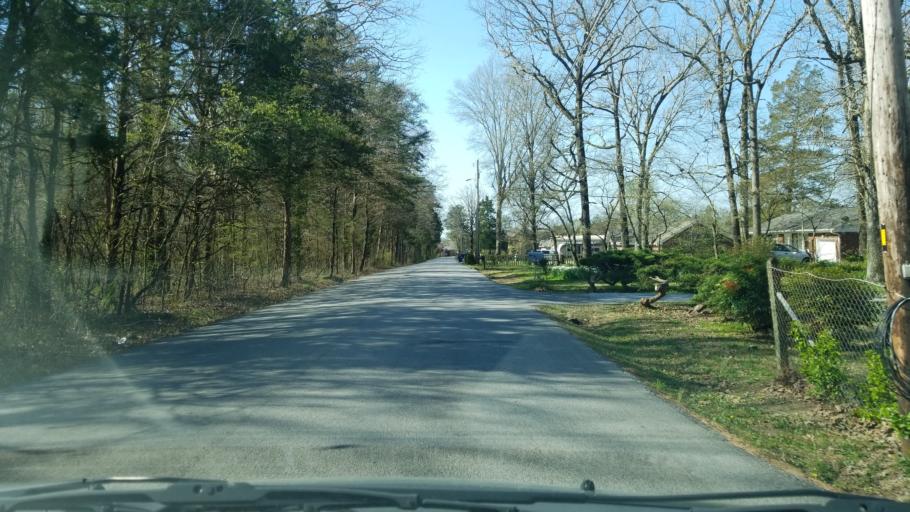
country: US
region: Tennessee
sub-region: Hamilton County
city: Harrison
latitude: 35.0623
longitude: -85.1447
